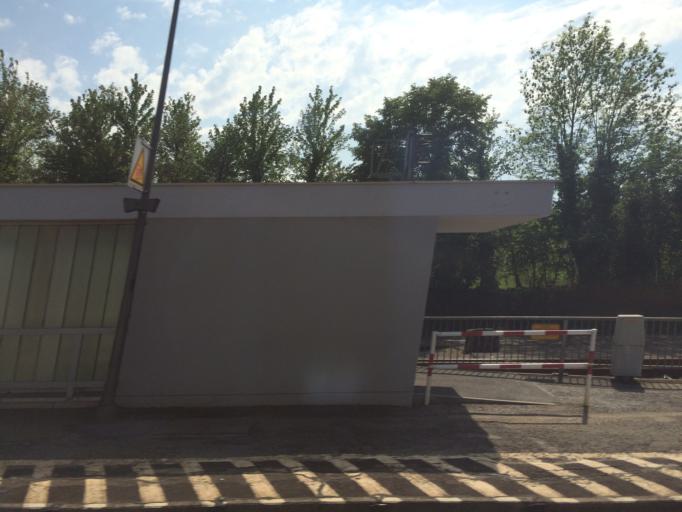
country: DE
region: Bavaria
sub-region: Regierungsbezirk Unterfranken
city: Iphofen
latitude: 49.6966
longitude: 10.2558
